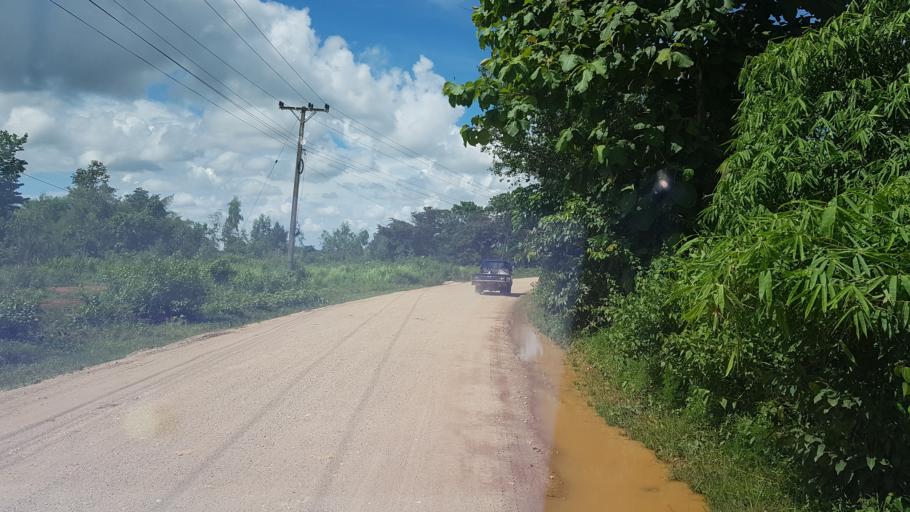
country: LA
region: Vientiane
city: Vientiane
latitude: 18.2310
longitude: 102.5260
